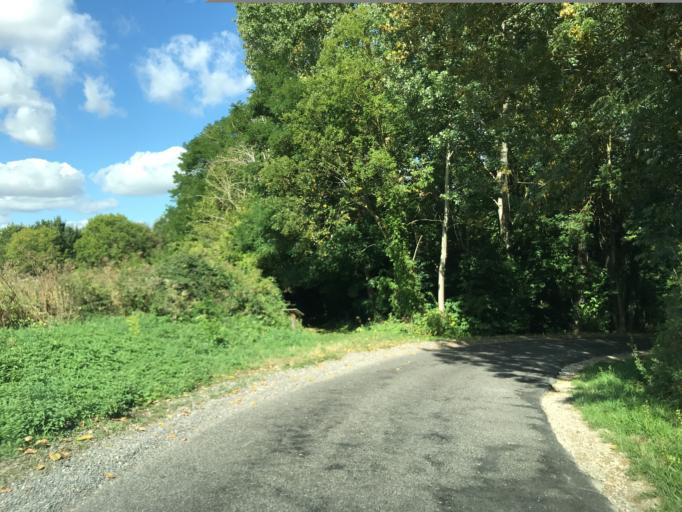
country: FR
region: Haute-Normandie
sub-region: Departement de l'Eure
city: La Chapelle-Reanville
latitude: 49.1082
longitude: 1.3852
